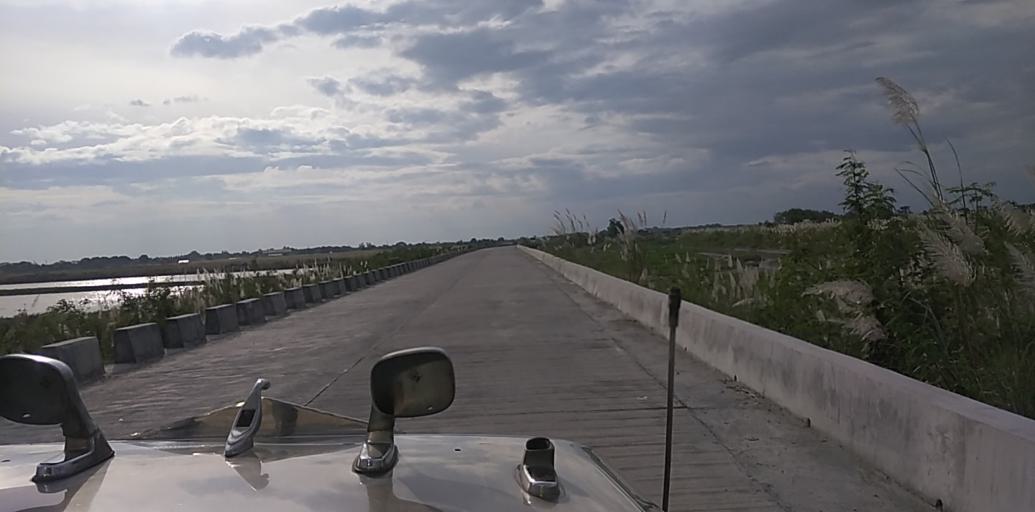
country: PH
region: Central Luzon
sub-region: Province of Pampanga
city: Minalin
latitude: 14.9671
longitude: 120.6711
